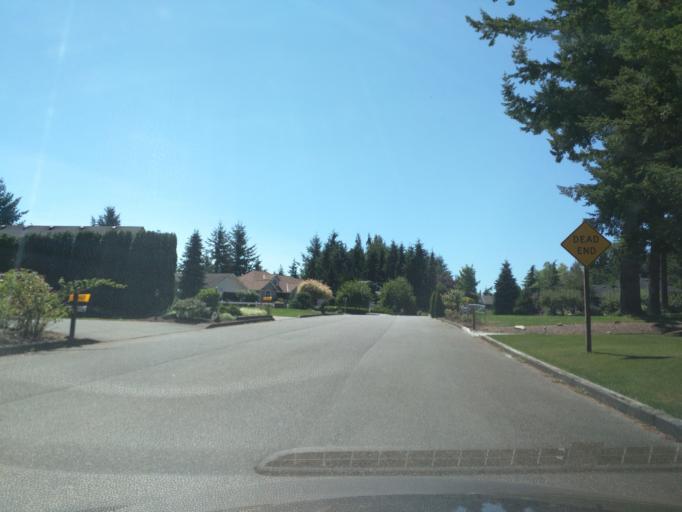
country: US
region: Washington
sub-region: Whatcom County
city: Lynden
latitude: 48.8916
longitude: -122.4471
